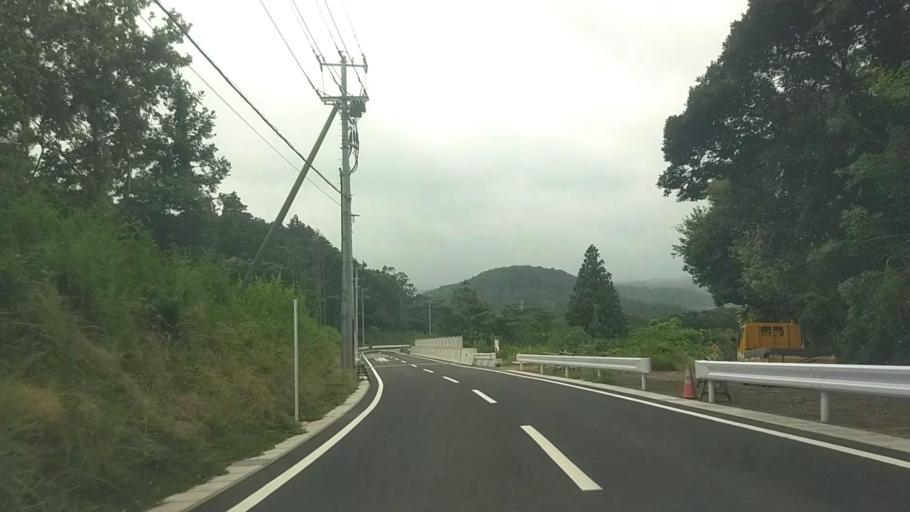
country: JP
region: Chiba
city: Kisarazu
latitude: 35.2639
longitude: 140.0494
